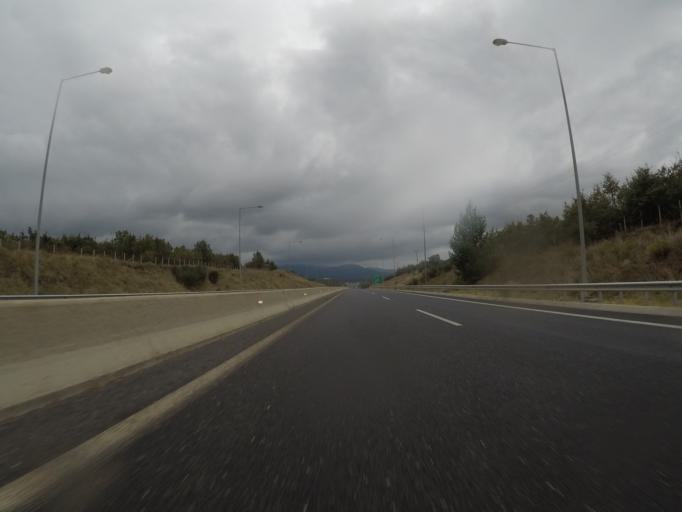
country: GR
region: Peloponnese
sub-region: Nomos Arkadias
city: Megalopoli
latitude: 37.3735
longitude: 22.1586
